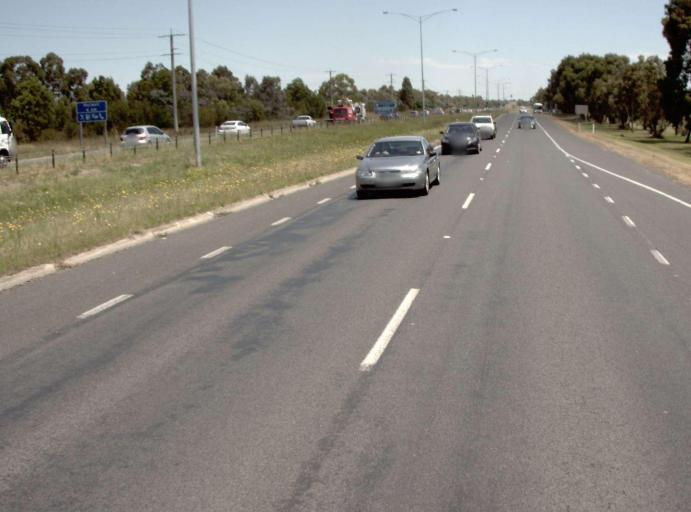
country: AU
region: Victoria
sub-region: Latrobe
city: Traralgon
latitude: -38.2185
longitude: 146.4749
